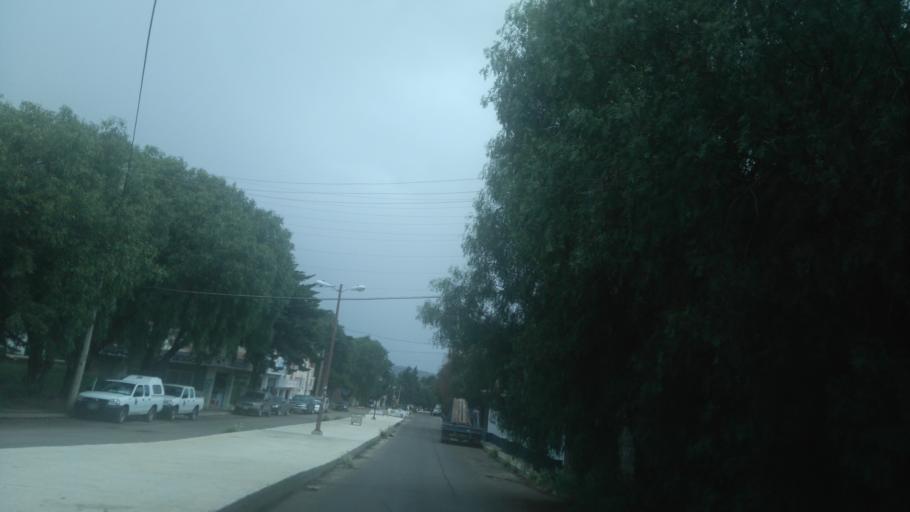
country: MX
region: Zacatecas
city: Zacatecas
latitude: 22.7582
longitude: -102.5873
